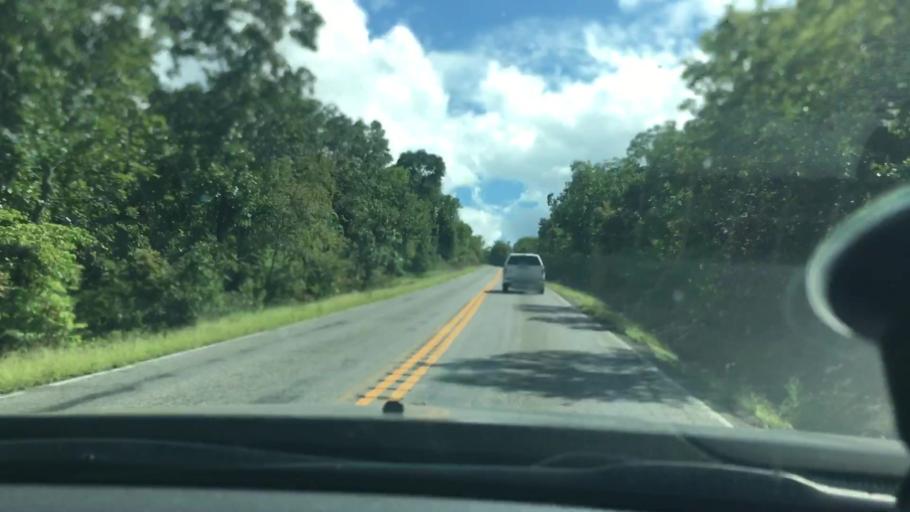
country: US
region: Oklahoma
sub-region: Sequoyah County
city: Vian
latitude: 35.6324
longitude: -94.9639
